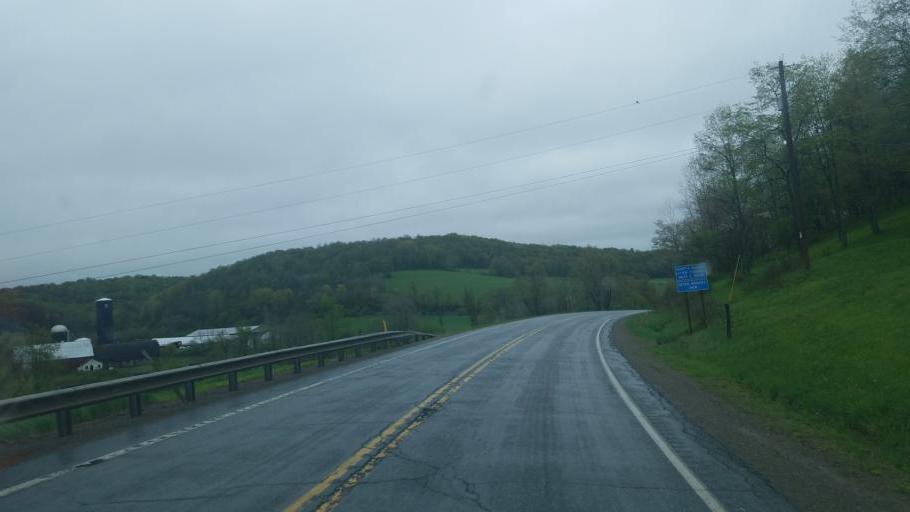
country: US
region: Pennsylvania
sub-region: Potter County
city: Coudersport
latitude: 41.8327
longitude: -77.9071
